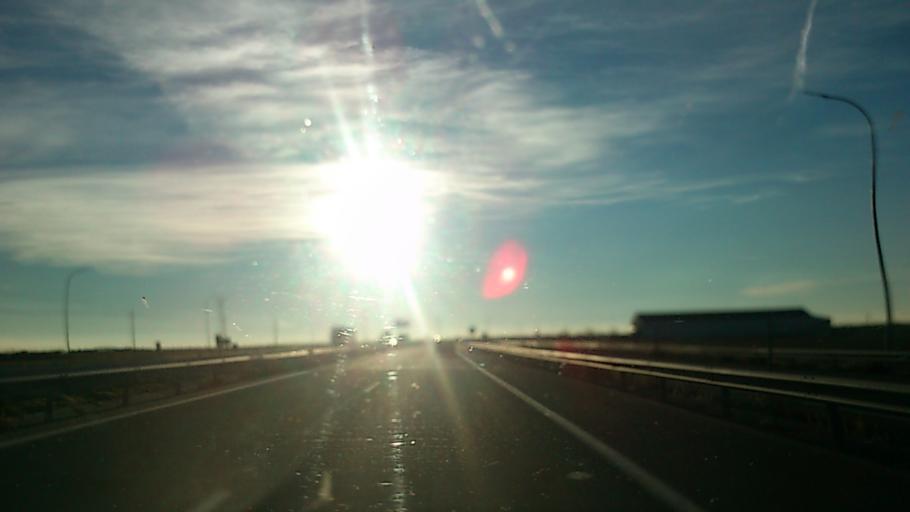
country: ES
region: Castille-La Mancha
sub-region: Provincia de Guadalajara
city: Ledanca
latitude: 40.8592
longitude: -2.8368
